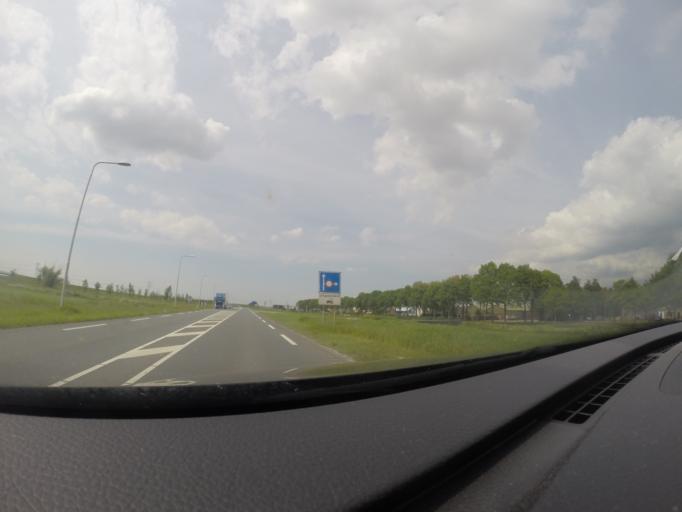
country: NL
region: Flevoland
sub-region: Gemeente Noordoostpolder
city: Ens
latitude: 52.6364
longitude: 5.8214
